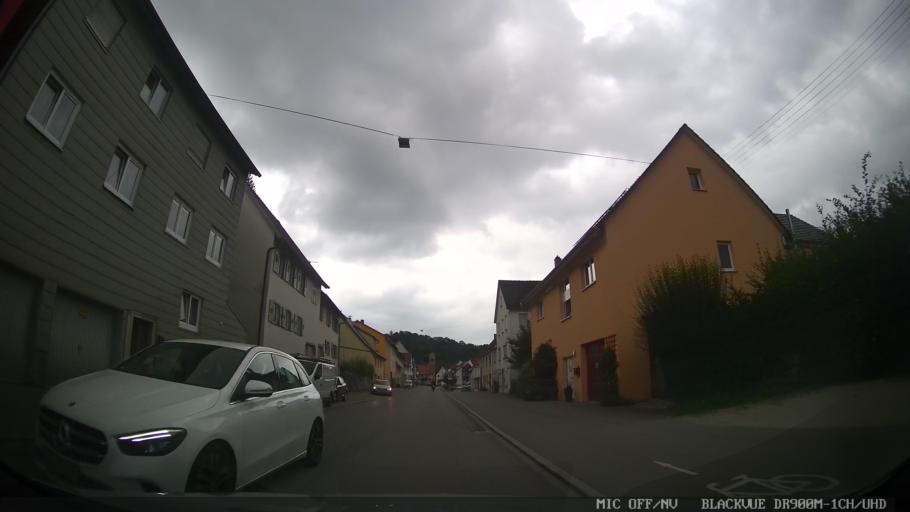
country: DE
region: Baden-Wuerttemberg
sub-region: Freiburg Region
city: Fridingen an der Donau
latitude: 48.0239
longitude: 8.9341
